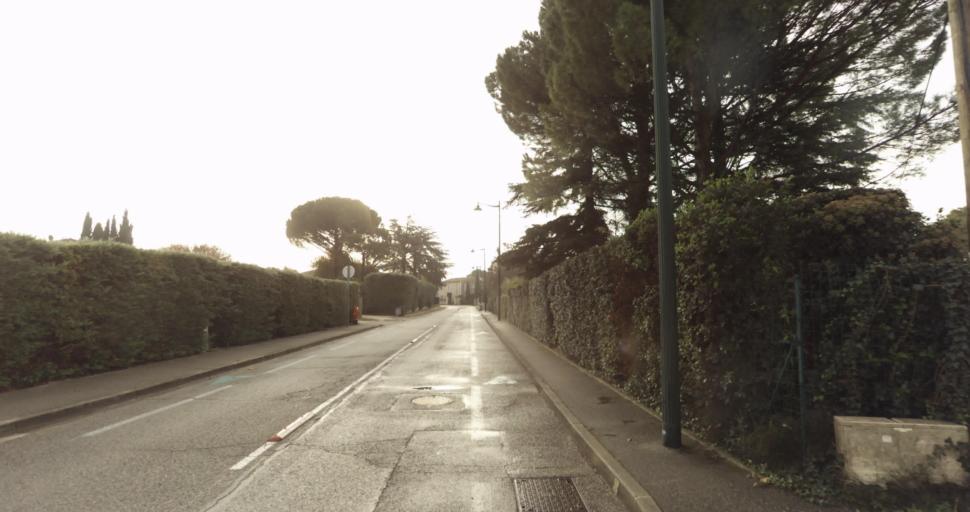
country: FR
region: Provence-Alpes-Cote d'Azur
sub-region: Departement des Bouches-du-Rhone
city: Rognonas
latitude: 43.9030
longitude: 4.7985
